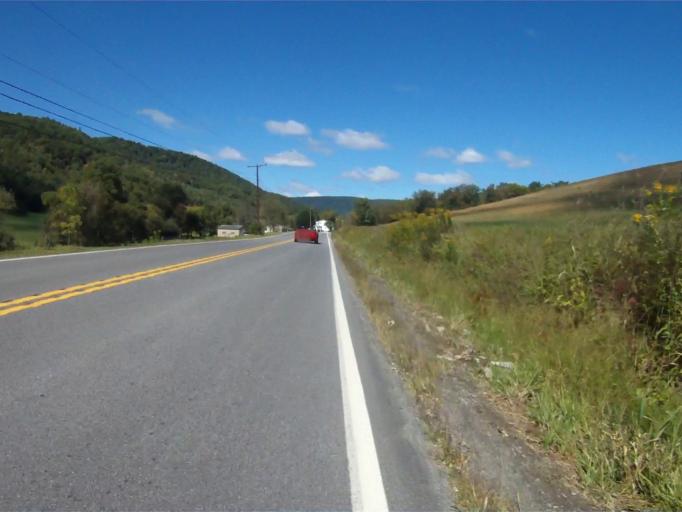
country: US
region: Pennsylvania
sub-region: Centre County
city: Houserville
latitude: 40.9100
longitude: -77.8828
